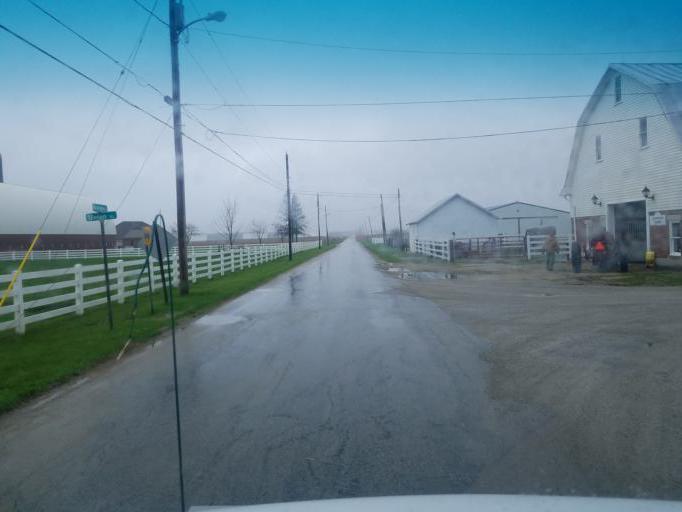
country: US
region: Ohio
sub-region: Wood County
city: North Baltimore
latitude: 41.2390
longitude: -83.6403
